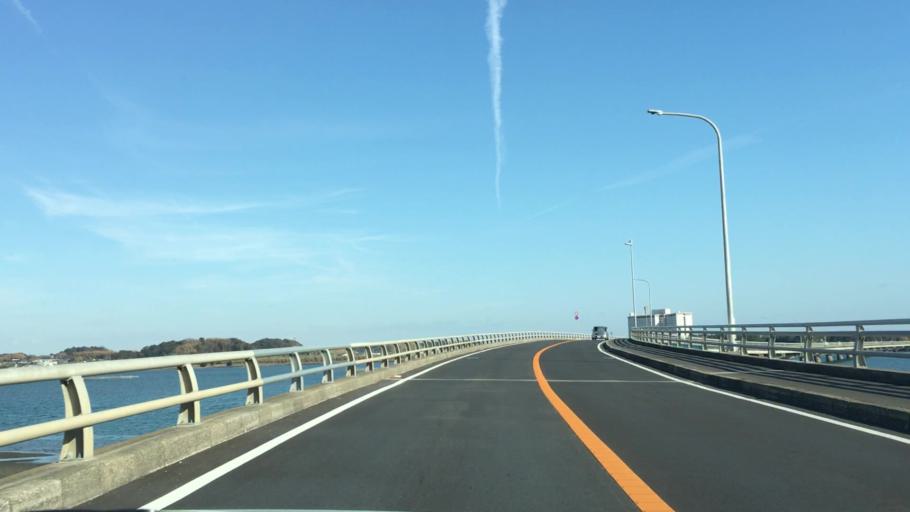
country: JP
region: Shizuoka
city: Kosai-shi
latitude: 34.7125
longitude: 137.6036
